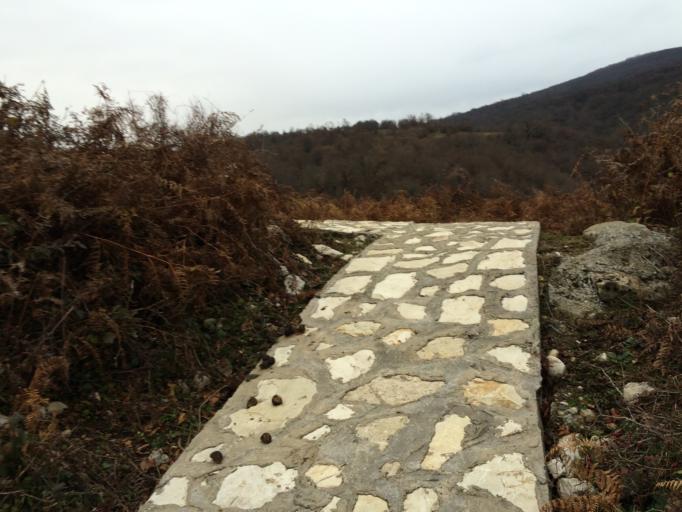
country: GE
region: Imereti
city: Tsqaltubo
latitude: 42.4557
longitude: 42.5465
